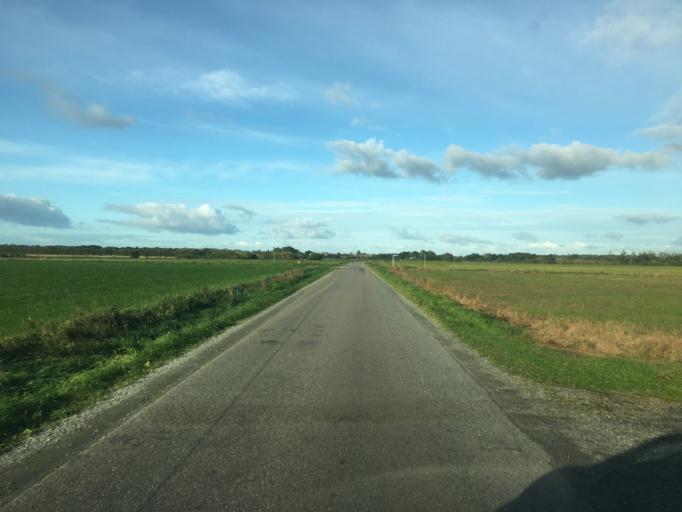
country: DK
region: South Denmark
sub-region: Tonder Kommune
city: Logumkloster
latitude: 55.0738
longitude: 8.9710
